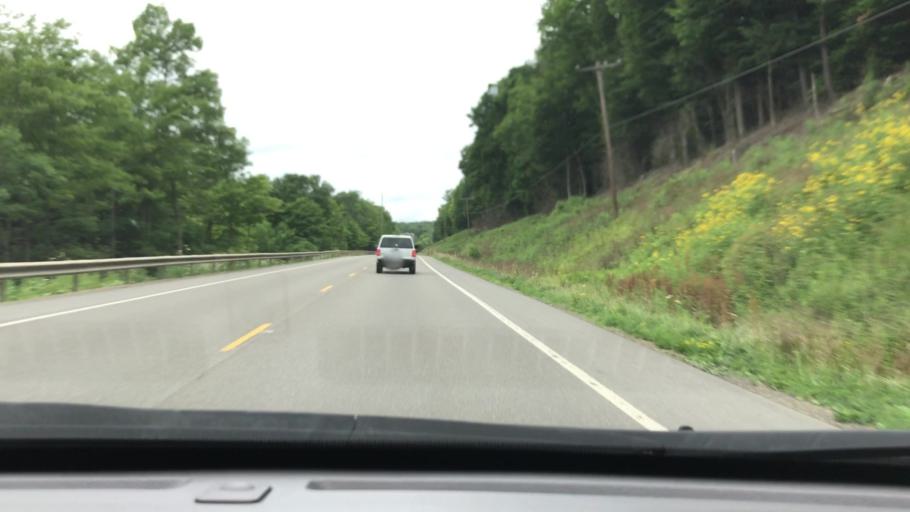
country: US
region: Pennsylvania
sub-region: McKean County
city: Kane
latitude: 41.6894
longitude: -78.6900
